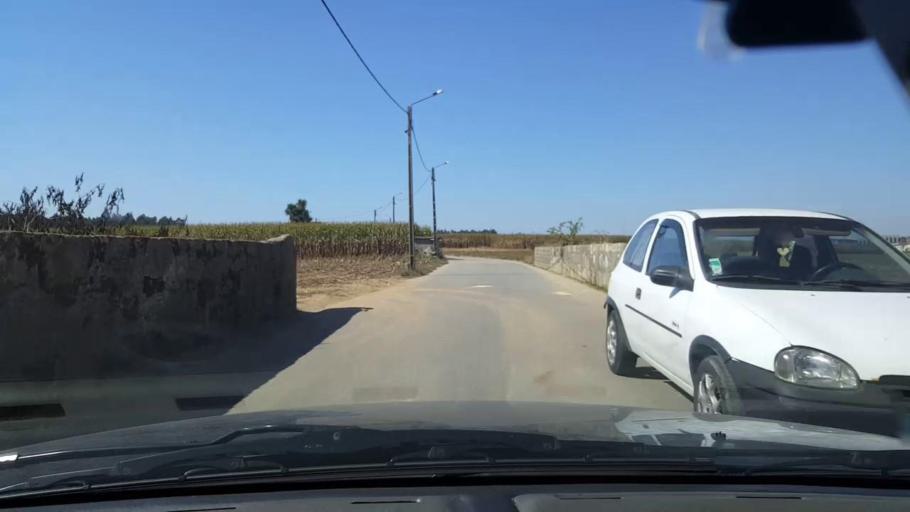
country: PT
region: Porto
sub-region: Matosinhos
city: Lavra
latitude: 41.2893
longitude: -8.6923
